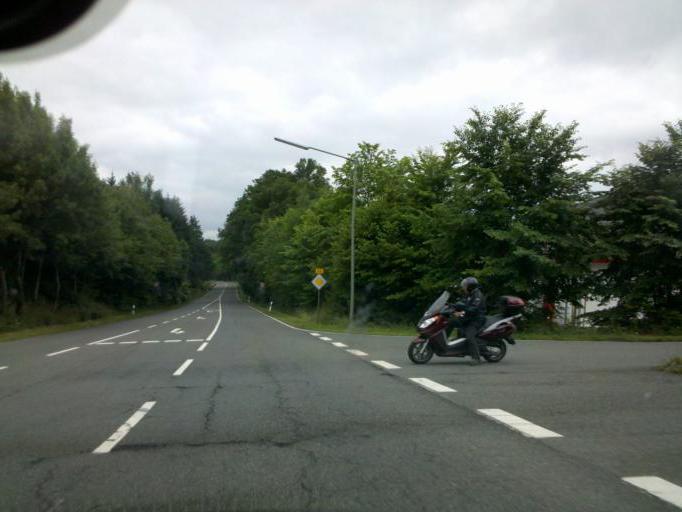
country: DE
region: North Rhine-Westphalia
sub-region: Regierungsbezirk Arnsberg
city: Wilnsdorf
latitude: 50.8403
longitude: 8.0725
